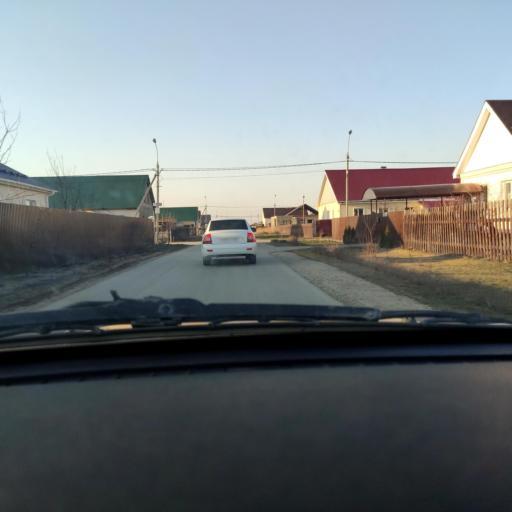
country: RU
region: Samara
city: Podstepki
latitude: 53.5738
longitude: 49.1131
